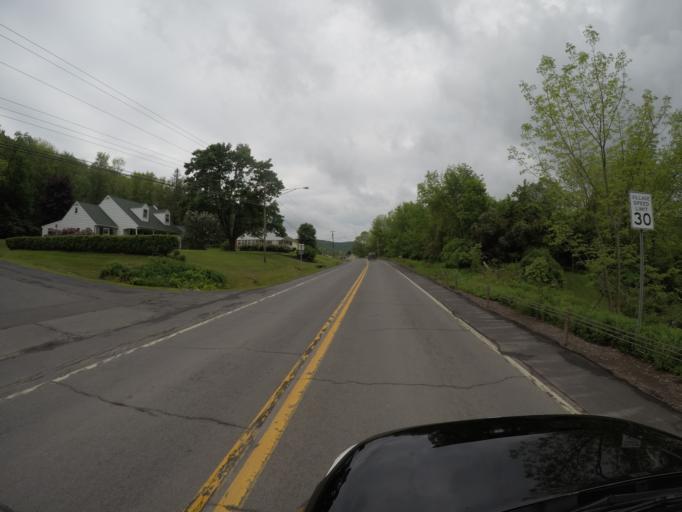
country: US
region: New York
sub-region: Delaware County
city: Delhi
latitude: 42.2670
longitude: -74.9167
